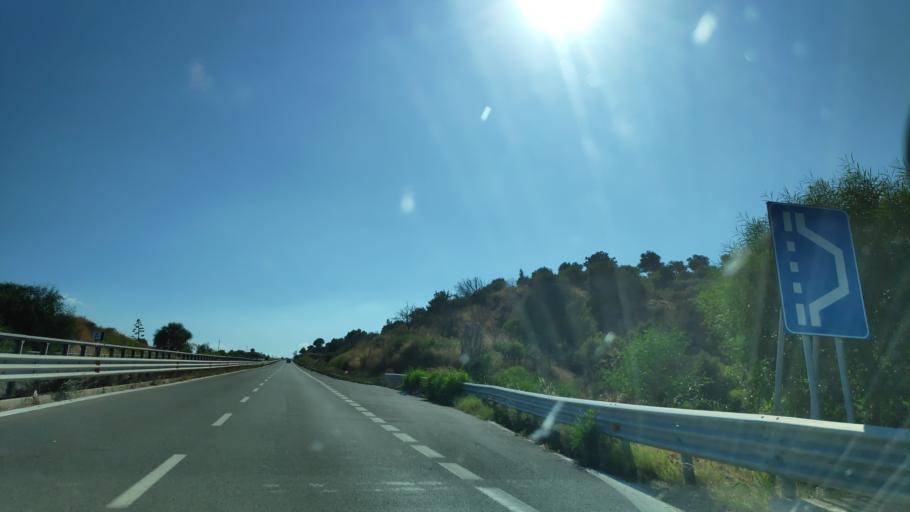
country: IT
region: Calabria
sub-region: Provincia di Reggio Calabria
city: Roccella Ionica
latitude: 38.3315
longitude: 16.4260
